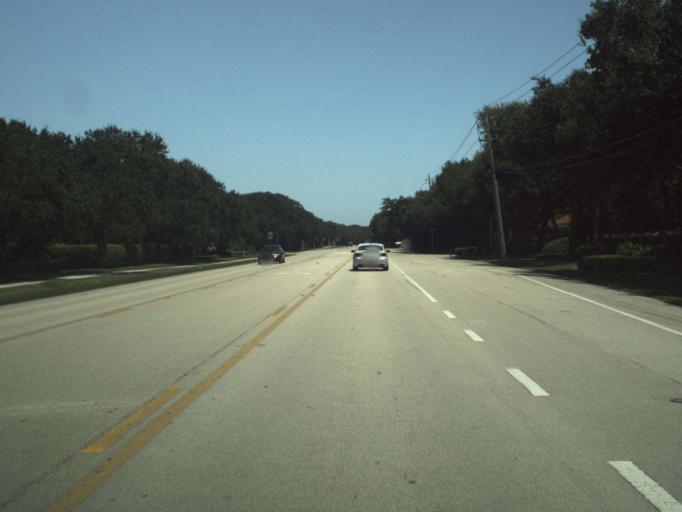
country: US
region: Florida
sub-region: Indian River County
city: Indian River Shores
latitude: 27.6958
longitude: -80.3725
